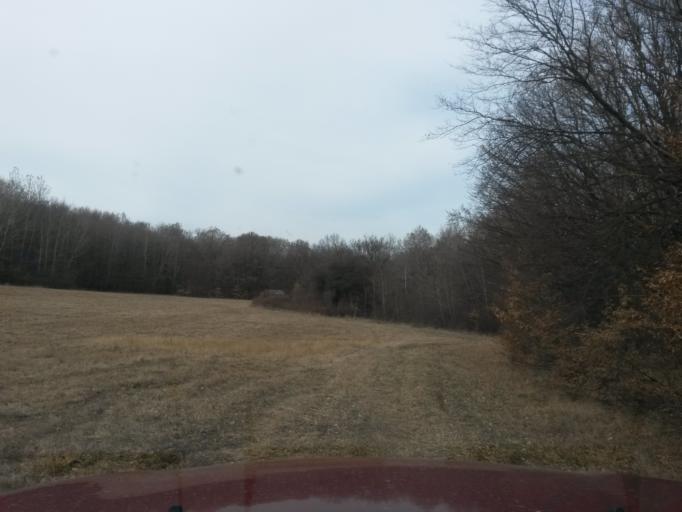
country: HU
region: Borsod-Abauj-Zemplen
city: Gonc
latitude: 48.5763
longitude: 21.3884
